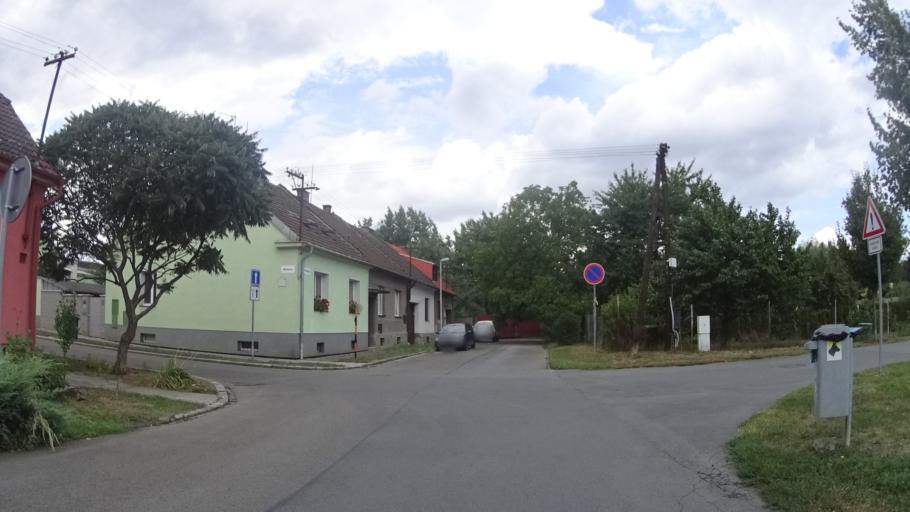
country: CZ
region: Olomoucky
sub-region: Okres Olomouc
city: Olomouc
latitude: 49.6102
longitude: 17.2345
